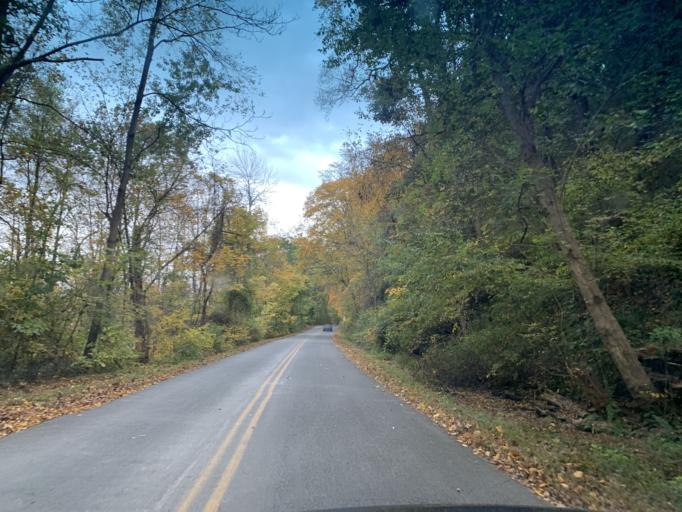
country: US
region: Maryland
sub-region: Harford County
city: Havre de Grace
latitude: 39.6125
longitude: -76.1487
